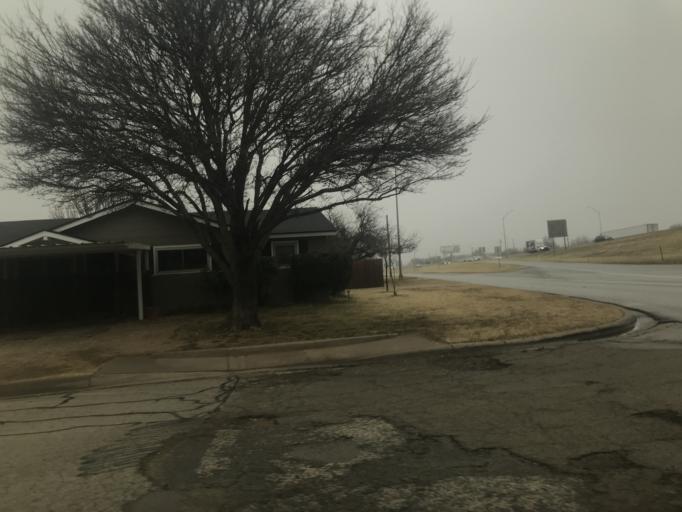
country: US
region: Texas
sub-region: Taylor County
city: Abilene
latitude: 32.4449
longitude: -99.7877
